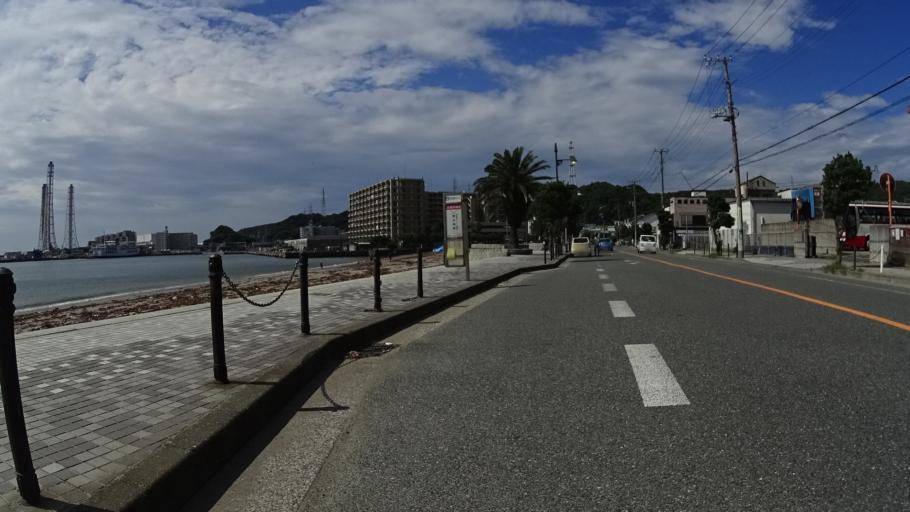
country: JP
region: Kanagawa
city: Yokosuka
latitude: 35.2255
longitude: 139.7137
